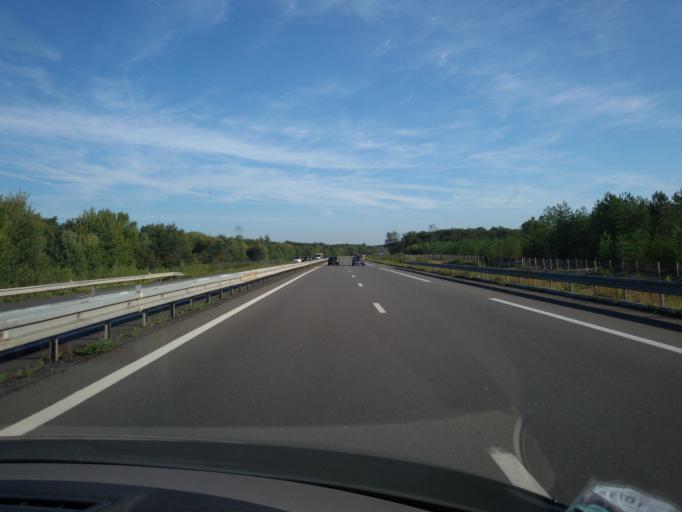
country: FR
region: Centre
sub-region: Departement du Loir-et-Cher
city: Theillay
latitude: 47.3316
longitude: 2.0481
